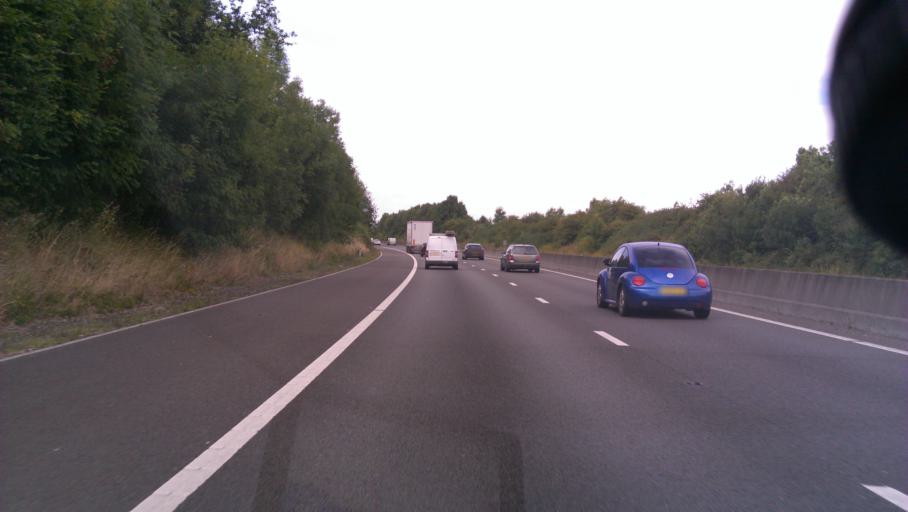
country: GB
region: England
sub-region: Essex
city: Elsenham
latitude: 51.9327
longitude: 0.2244
